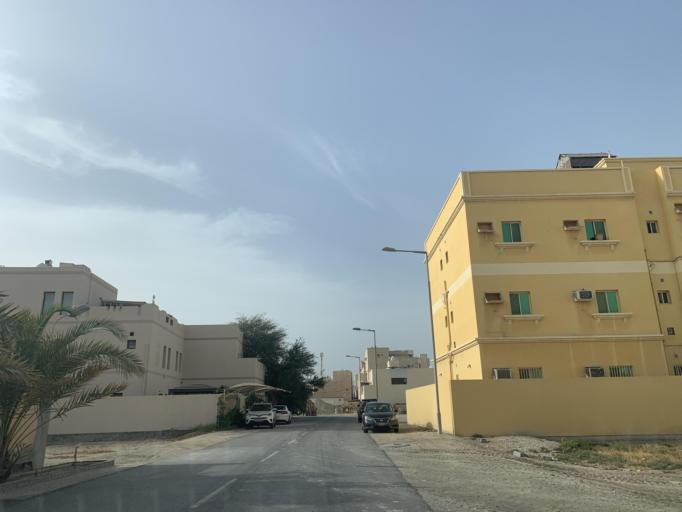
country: BH
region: Central Governorate
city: Madinat Hamad
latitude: 26.1543
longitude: 50.5081
